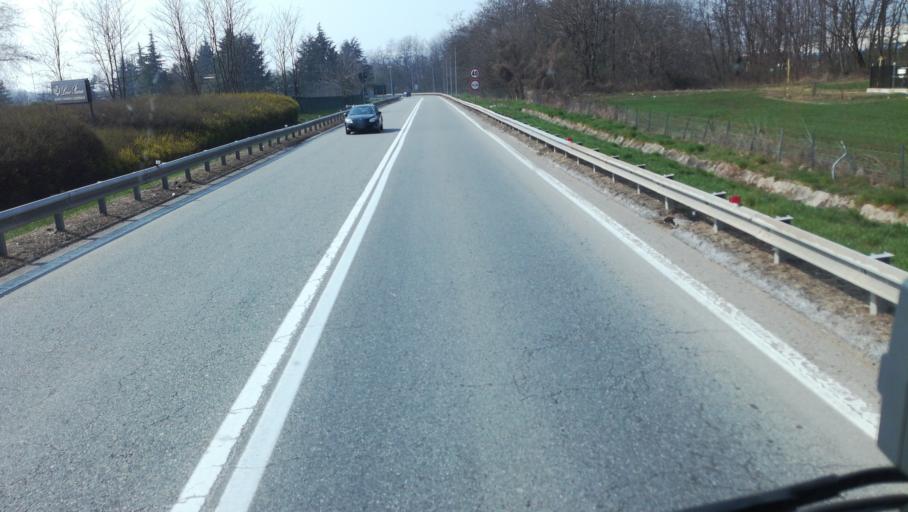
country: IT
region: Piedmont
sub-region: Provincia di Novara
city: Ghemme
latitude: 45.6123
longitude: 8.4072
